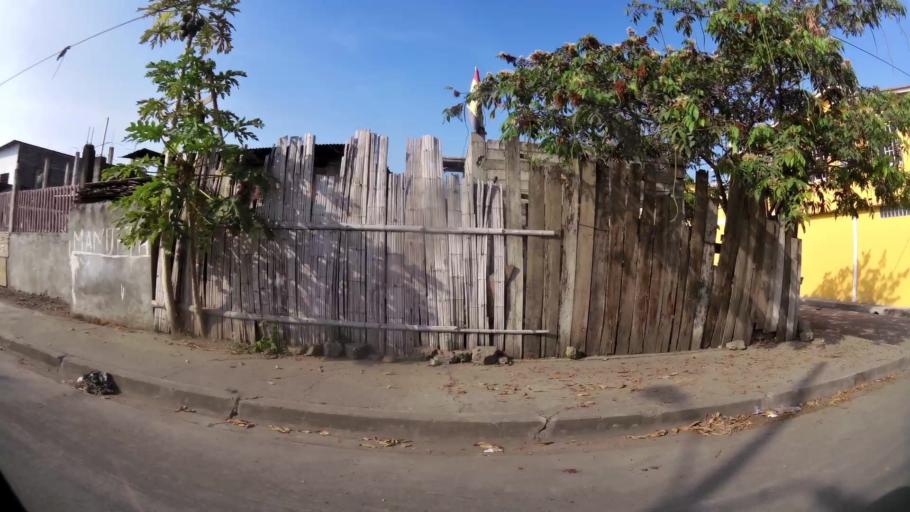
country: EC
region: Guayas
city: Eloy Alfaro
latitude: -2.1822
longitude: -79.8376
